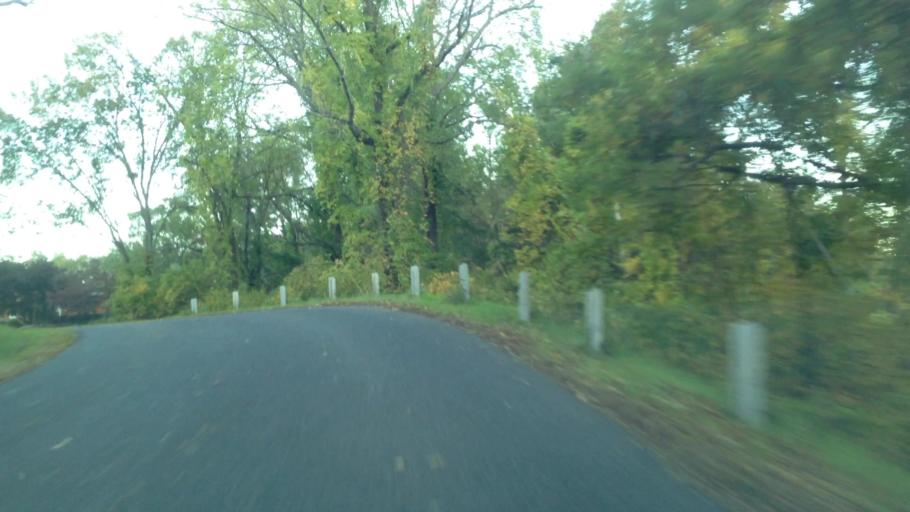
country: US
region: New York
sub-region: Dutchess County
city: Hyde Park
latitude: 41.8074
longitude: -73.9776
